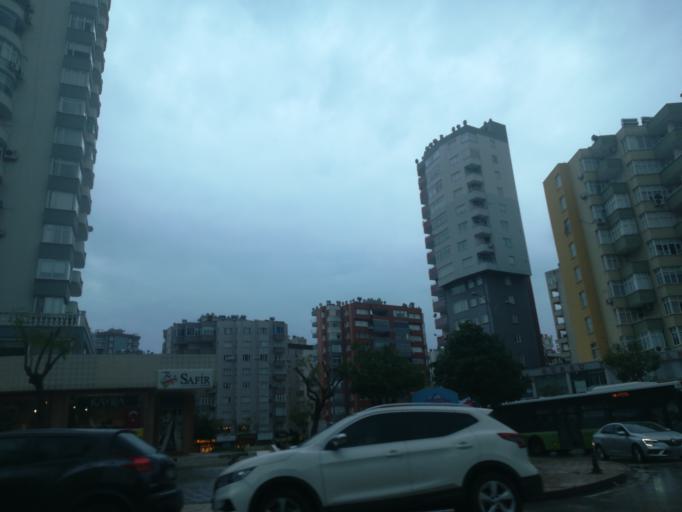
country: TR
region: Adana
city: Adana
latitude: 37.0476
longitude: 35.2994
